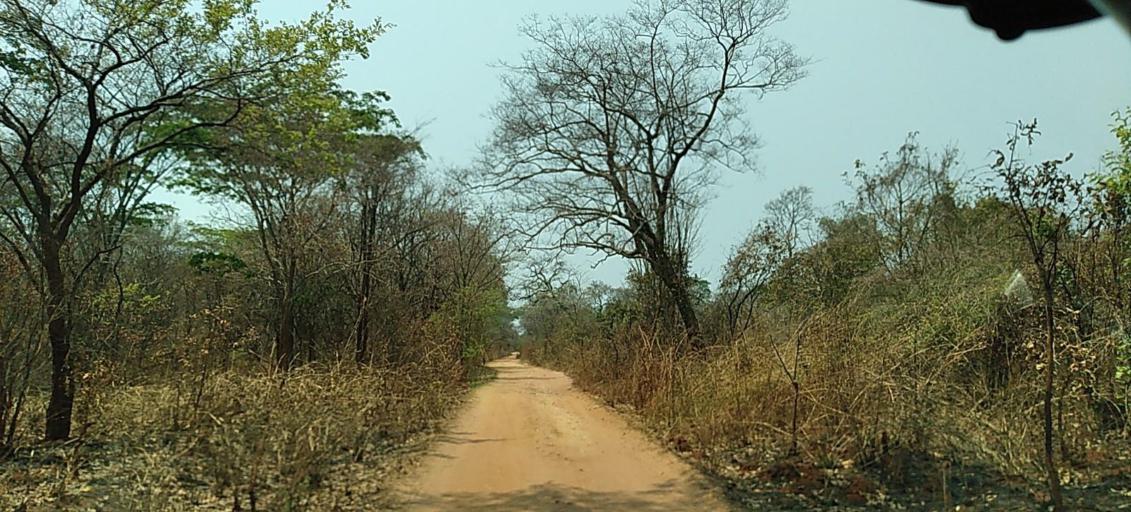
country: ZM
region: North-Western
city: Kabompo
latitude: -13.7002
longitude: 24.3168
